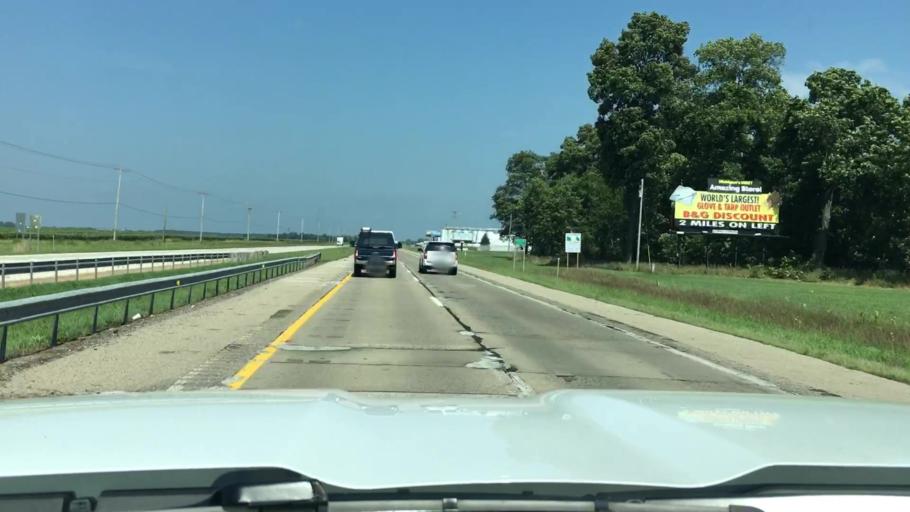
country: US
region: Michigan
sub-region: Kalamazoo County
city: Schoolcraft
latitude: 42.0698
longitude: -85.6363
